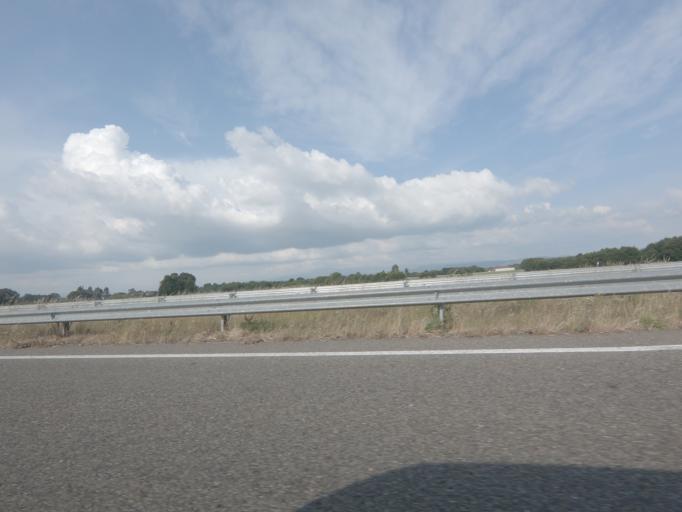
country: ES
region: Galicia
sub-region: Provincia de Ourense
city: Xinzo de Limia
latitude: 42.1165
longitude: -7.7380
